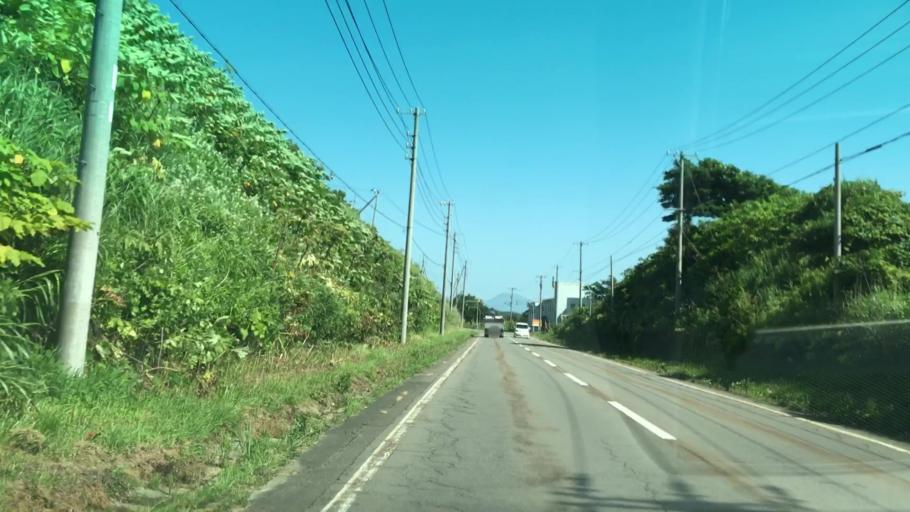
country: JP
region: Hokkaido
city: Iwanai
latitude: 43.0807
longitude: 140.4786
